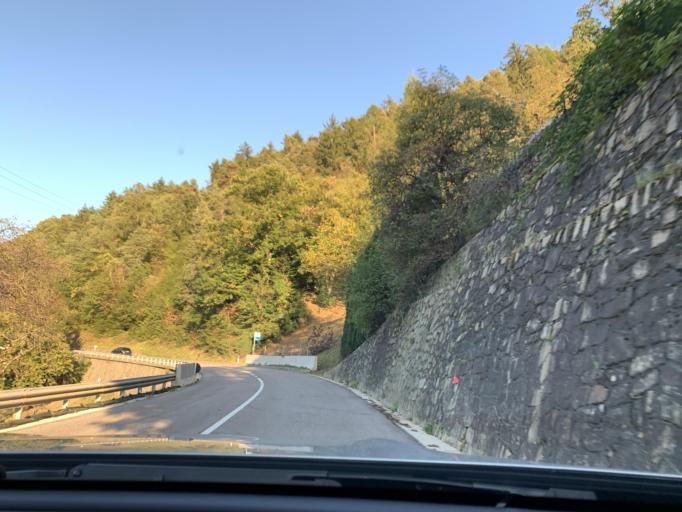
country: IT
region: Trentino-Alto Adige
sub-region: Bolzano
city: Fie Allo Sciliar
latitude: 46.5031
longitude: 11.4664
